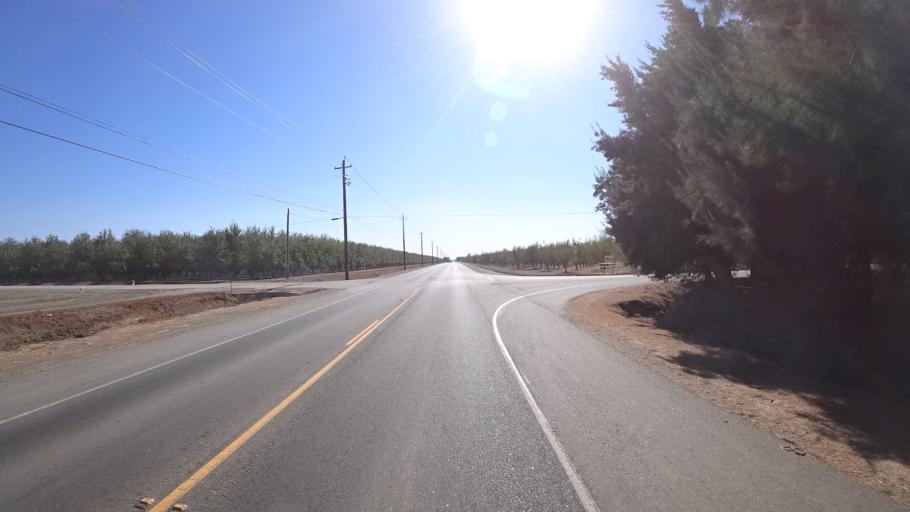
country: US
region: California
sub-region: Yolo County
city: Woodland
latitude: 38.6055
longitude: -121.8031
